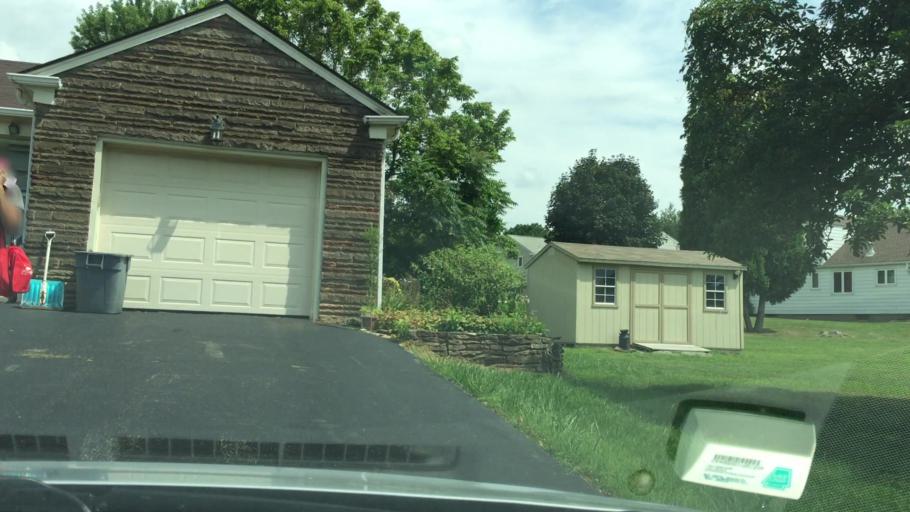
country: US
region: Pennsylvania
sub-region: Beaver County
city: Beaver
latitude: 40.7080
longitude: -80.3168
